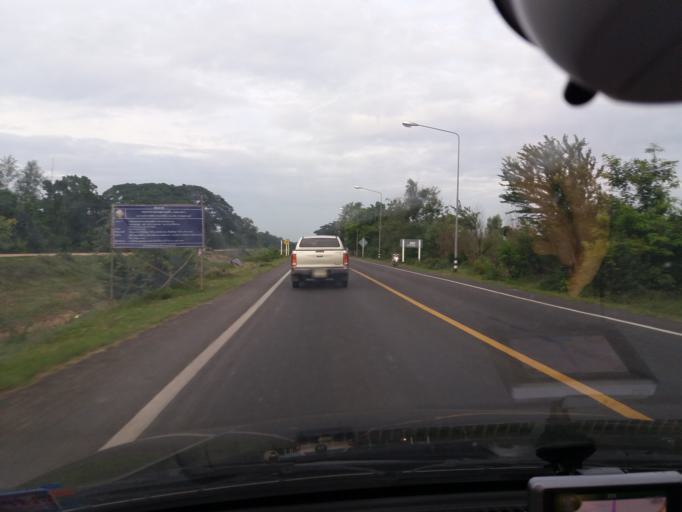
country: TH
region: Suphan Buri
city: Don Chedi
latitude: 14.5317
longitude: 99.9322
